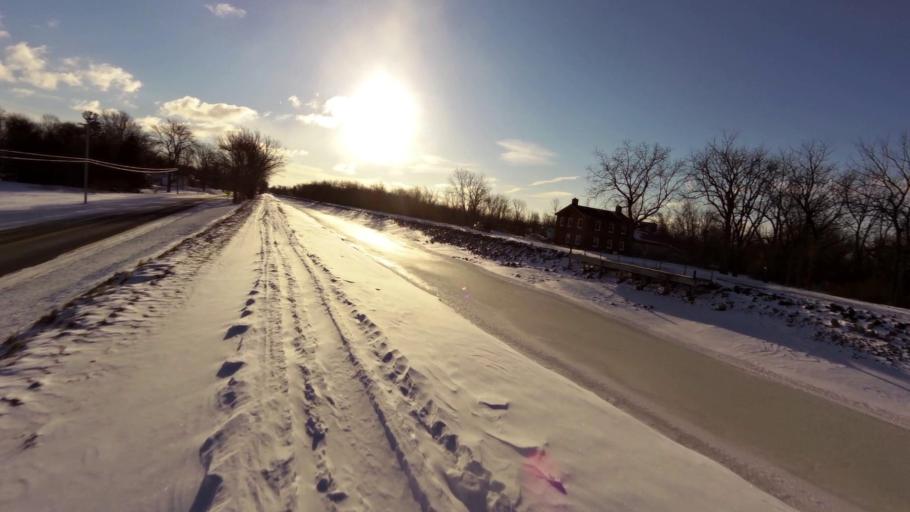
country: US
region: New York
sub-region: Orleans County
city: Albion
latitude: 43.2518
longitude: -78.2633
